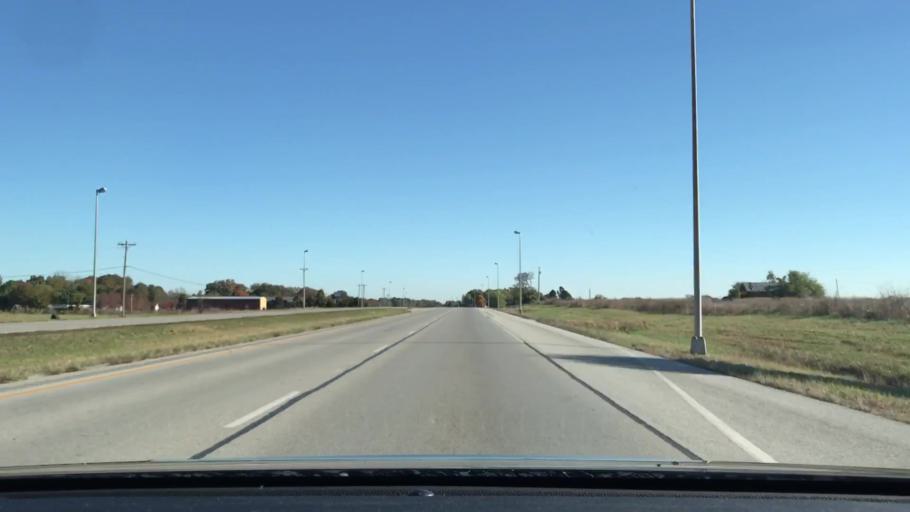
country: US
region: Kentucky
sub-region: Warren County
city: Bowling Green
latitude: 36.9442
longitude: -86.5239
